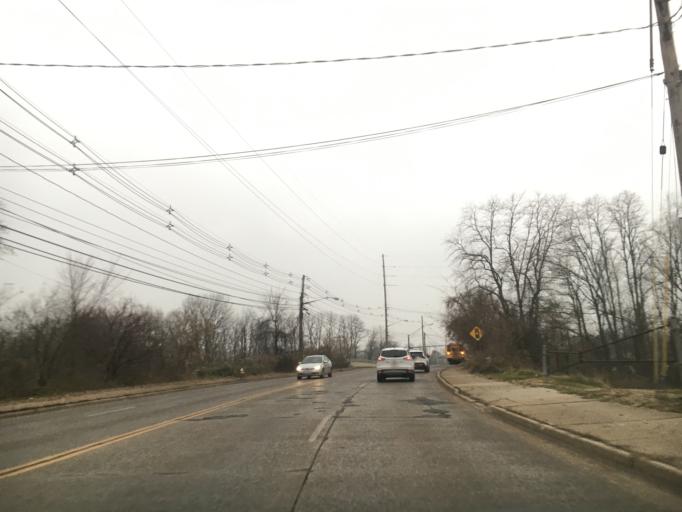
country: US
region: Ohio
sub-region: Summit County
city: Akron
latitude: 41.0867
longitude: -81.4905
